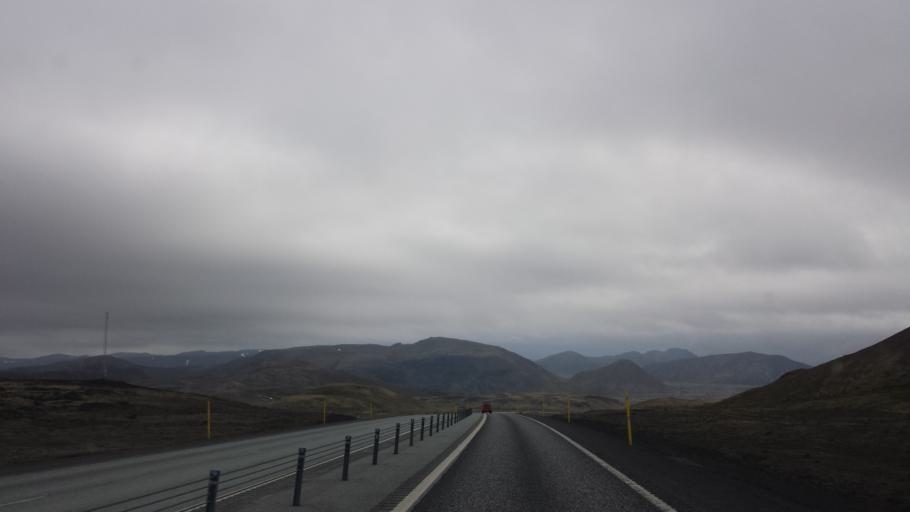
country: IS
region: South
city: THorlakshoefn
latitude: 64.0188
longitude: -21.3848
